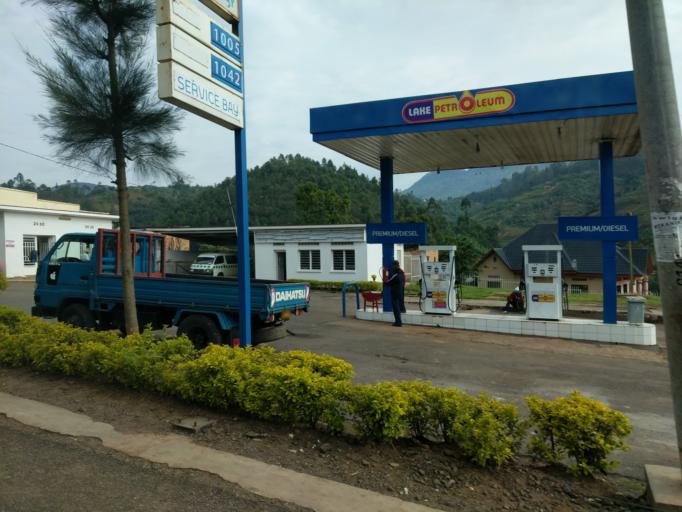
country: RW
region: Northern Province
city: Musanze
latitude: -1.6480
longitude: 29.7929
